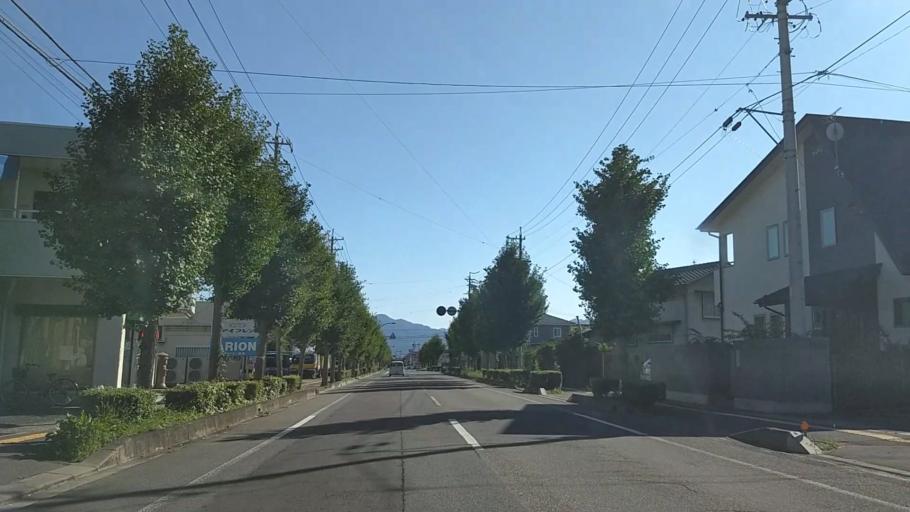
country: JP
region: Nagano
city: Nagano-shi
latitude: 36.5819
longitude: 138.1364
